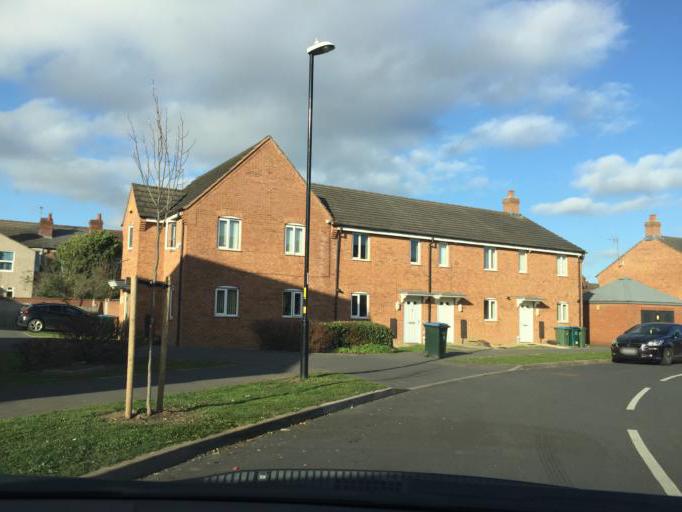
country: GB
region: England
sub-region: Coventry
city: Coventry
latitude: 52.4025
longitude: -1.4859
